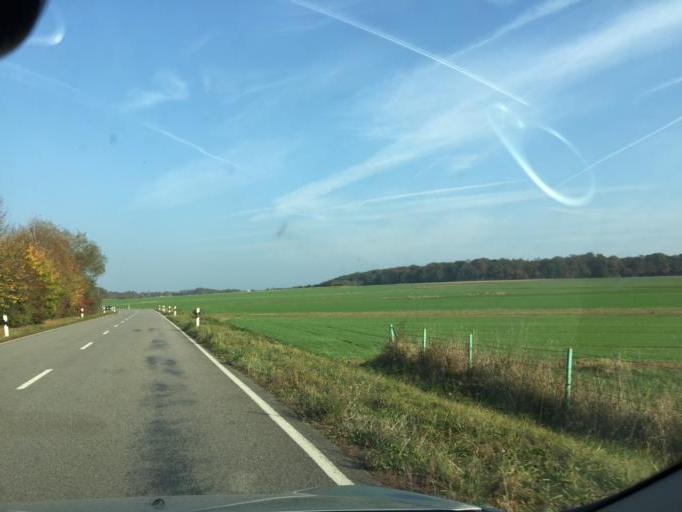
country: LU
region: Luxembourg
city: Aspelt
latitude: 49.5513
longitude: 6.2307
